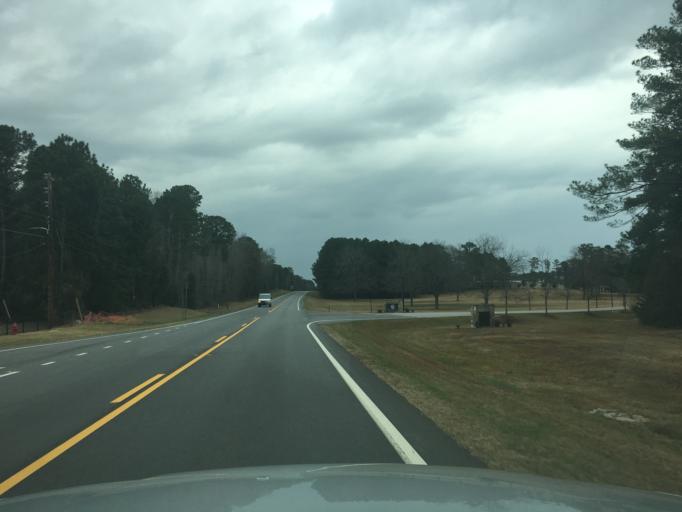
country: US
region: Georgia
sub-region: Columbia County
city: Appling
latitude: 33.6736
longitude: -82.3366
